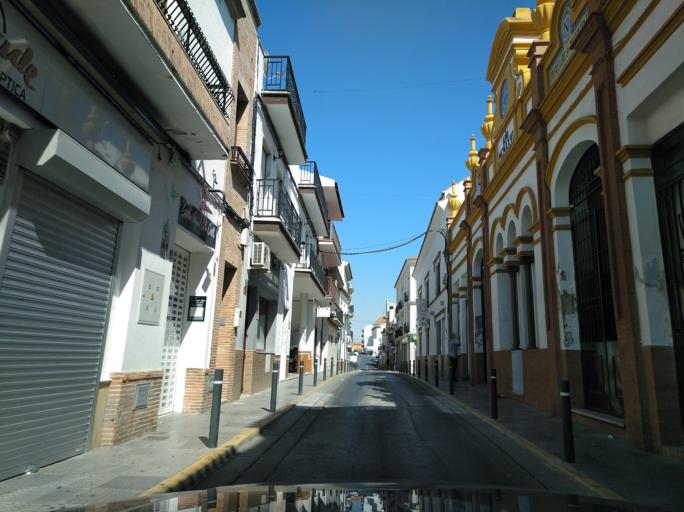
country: ES
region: Andalusia
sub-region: Provincia de Huelva
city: Gibraleon
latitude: 37.3757
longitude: -6.9696
